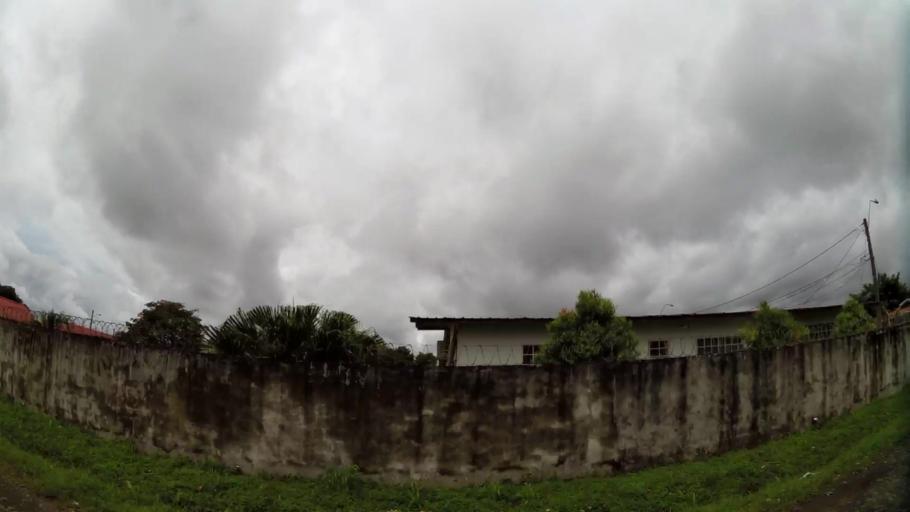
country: PA
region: Chiriqui
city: David
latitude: 8.4142
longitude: -82.4540
